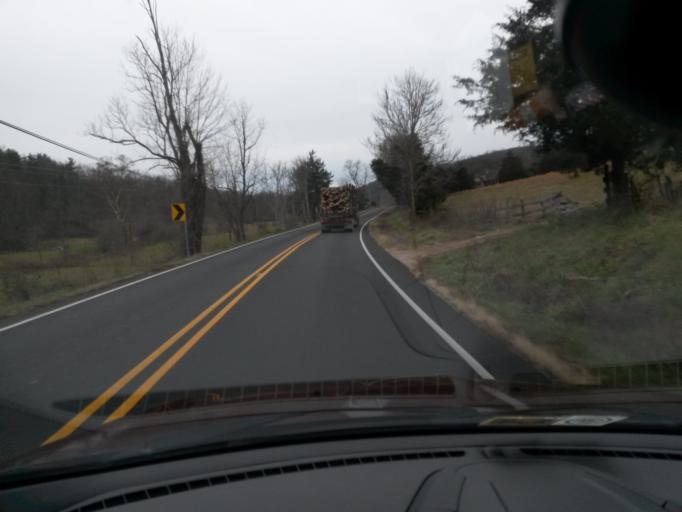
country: US
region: Virginia
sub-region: Amherst County
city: Amherst
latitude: 37.6599
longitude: -79.1543
